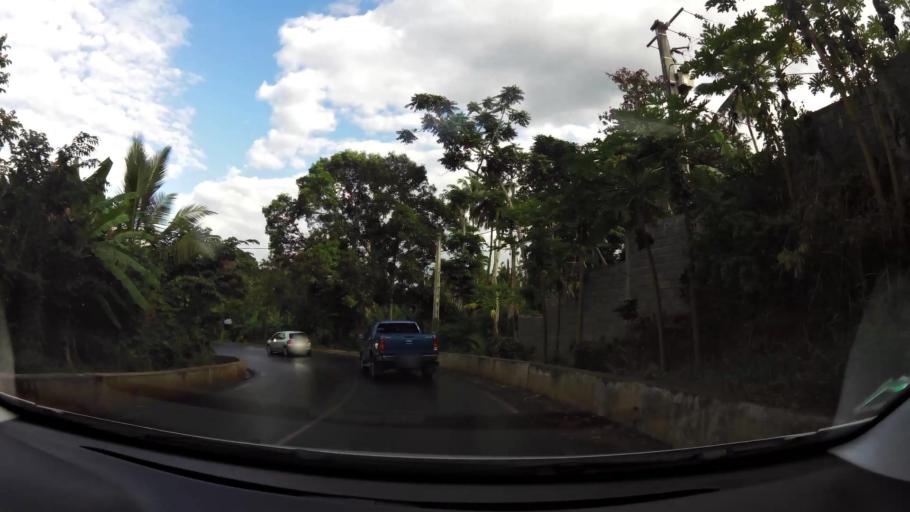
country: YT
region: Ouangani
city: Ouangani
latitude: -12.8358
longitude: 45.1455
